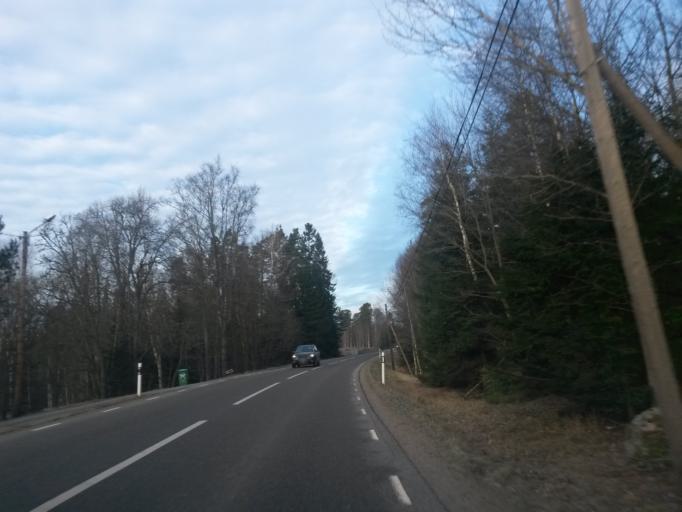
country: SE
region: Vaestra Goetaland
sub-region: Vargarda Kommun
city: Vargarda
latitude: 57.9049
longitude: 12.9075
